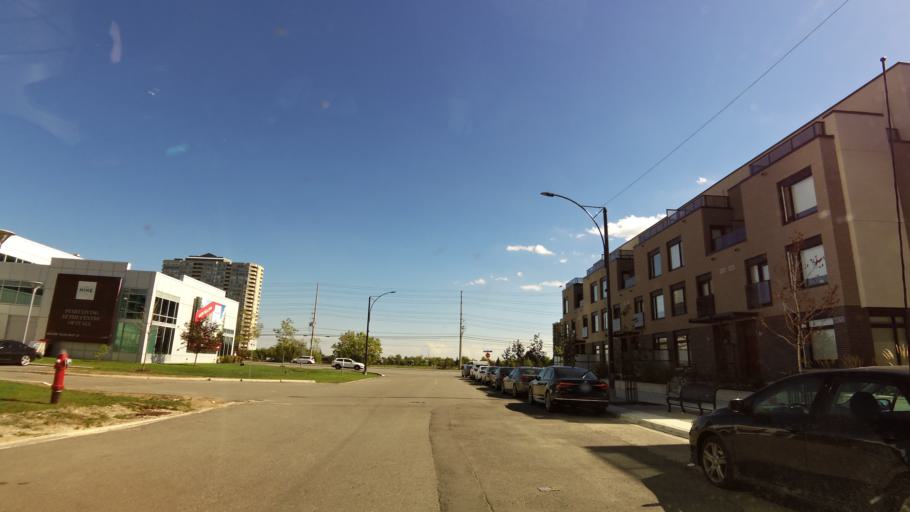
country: CA
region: Ontario
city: Mississauga
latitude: 43.5847
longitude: -79.6472
